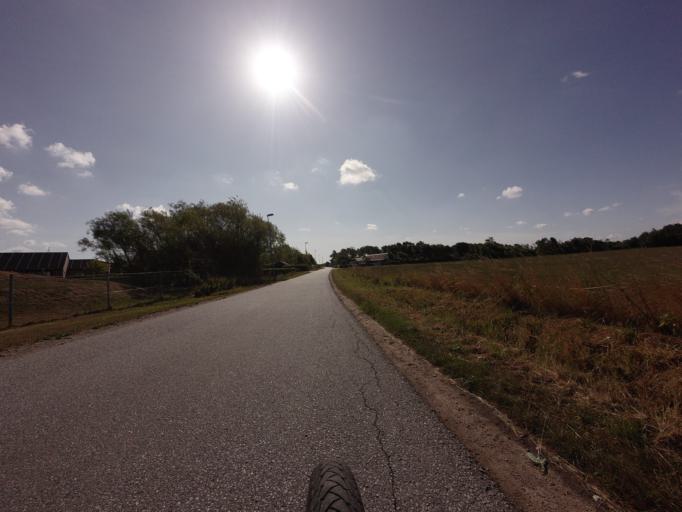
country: DK
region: North Denmark
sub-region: Hjorring Kommune
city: Vra
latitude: 57.3965
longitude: 9.9833
